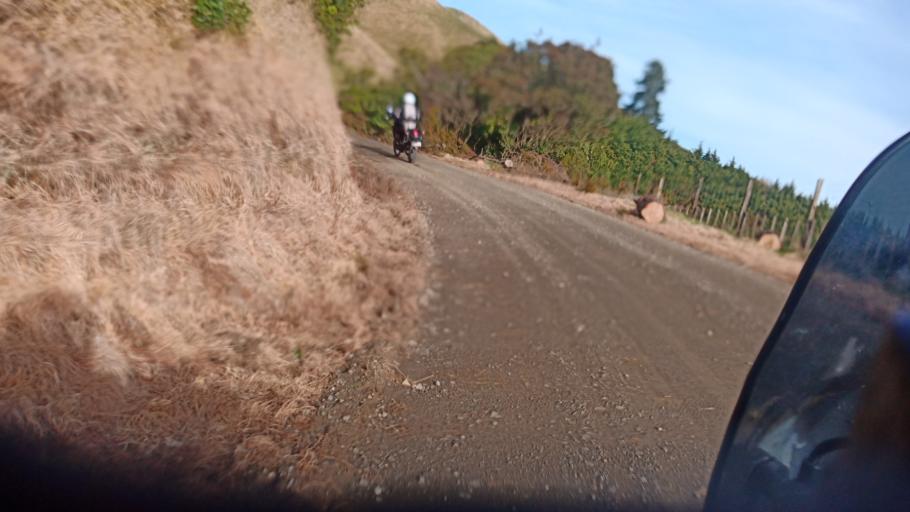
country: NZ
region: Bay of Plenty
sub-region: Opotiki District
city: Opotiki
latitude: -38.4486
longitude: 177.5391
